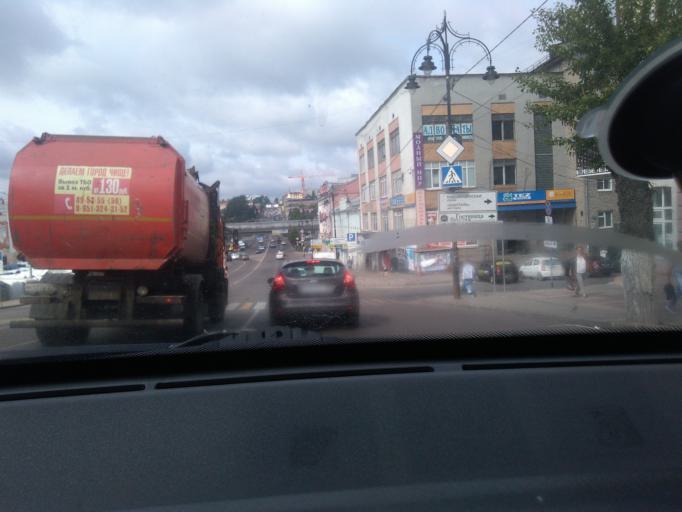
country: RU
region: Kursk
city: Kursk
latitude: 51.7282
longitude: 36.1882
